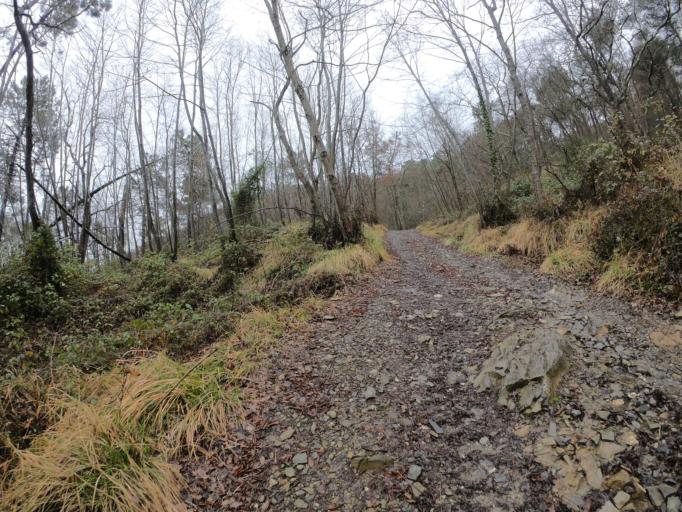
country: IT
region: Liguria
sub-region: Provincia di Imperia
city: Villa Faraldi
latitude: 43.9766
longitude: 8.1049
